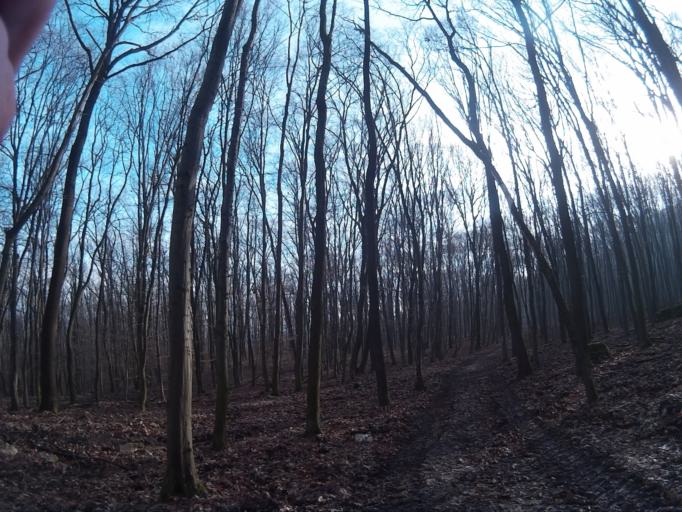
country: HU
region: Komarom-Esztergom
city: Tarjan
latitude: 47.6130
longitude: 18.4758
